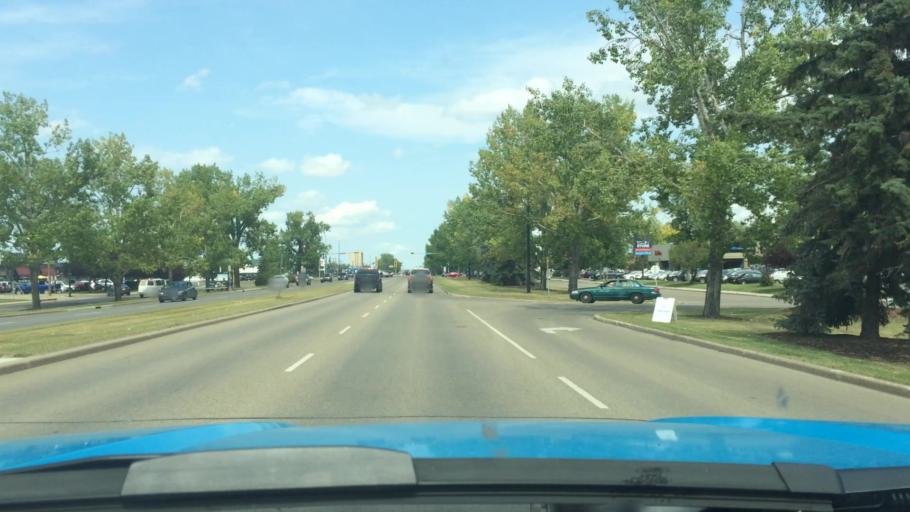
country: CA
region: Alberta
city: Red Deer
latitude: 52.2399
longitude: -113.8139
